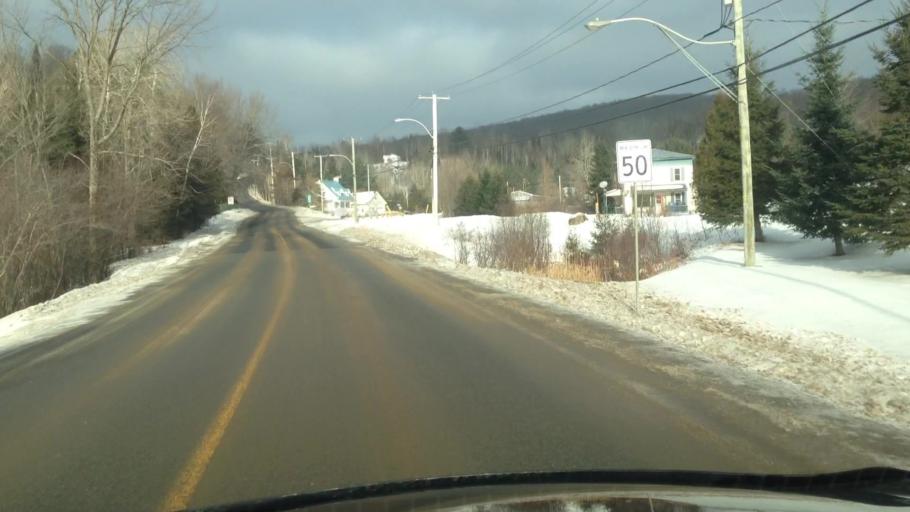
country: CA
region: Quebec
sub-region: Laurentides
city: Sainte-Agathe-des-Monts
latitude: 45.9246
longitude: -74.4666
